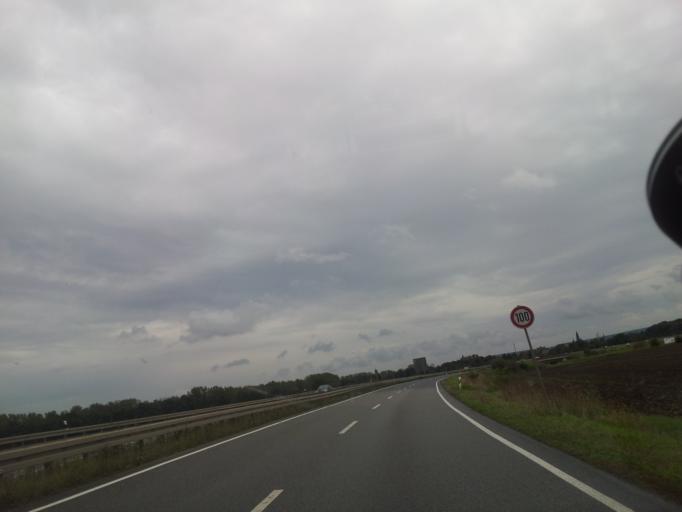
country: DE
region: Saxony-Anhalt
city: Egeln
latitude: 51.9549
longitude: 11.4453
